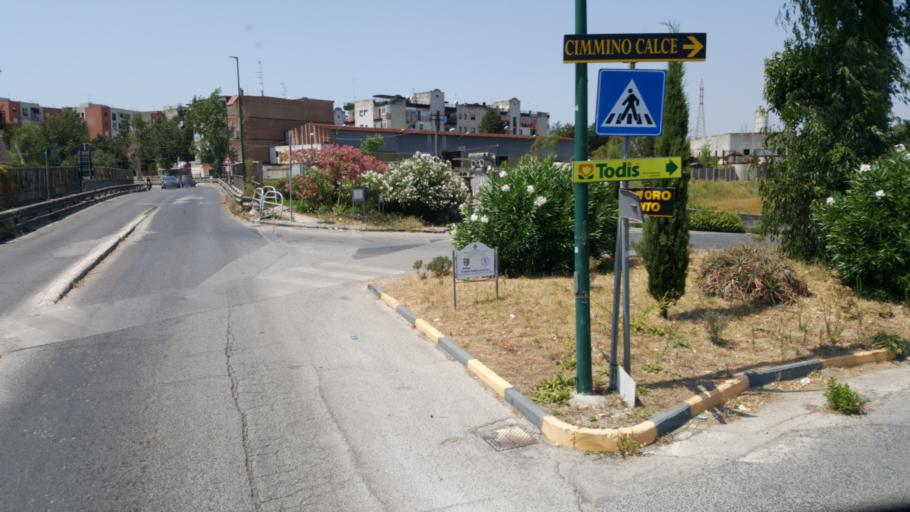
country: IT
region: Campania
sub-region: Provincia di Napoli
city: Arpino
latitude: 40.8841
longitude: 14.3136
